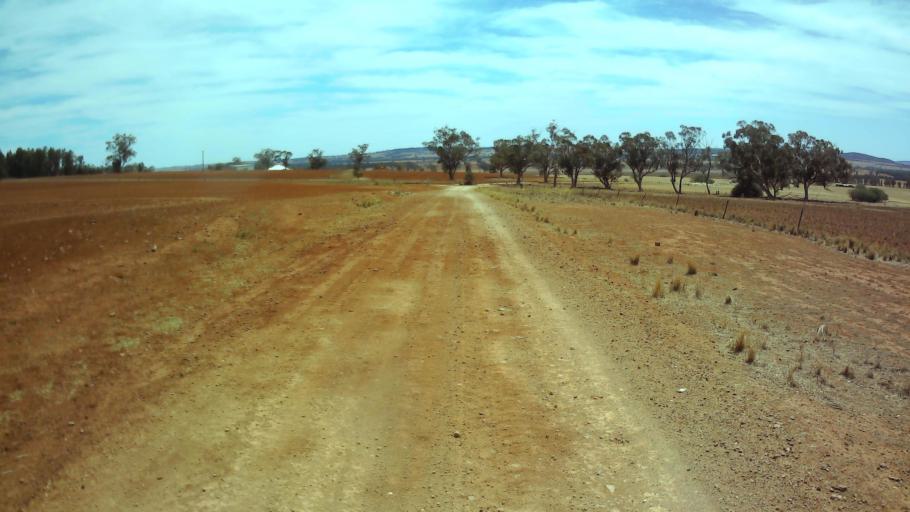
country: AU
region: New South Wales
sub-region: Weddin
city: Grenfell
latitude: -33.7499
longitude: 148.1585
